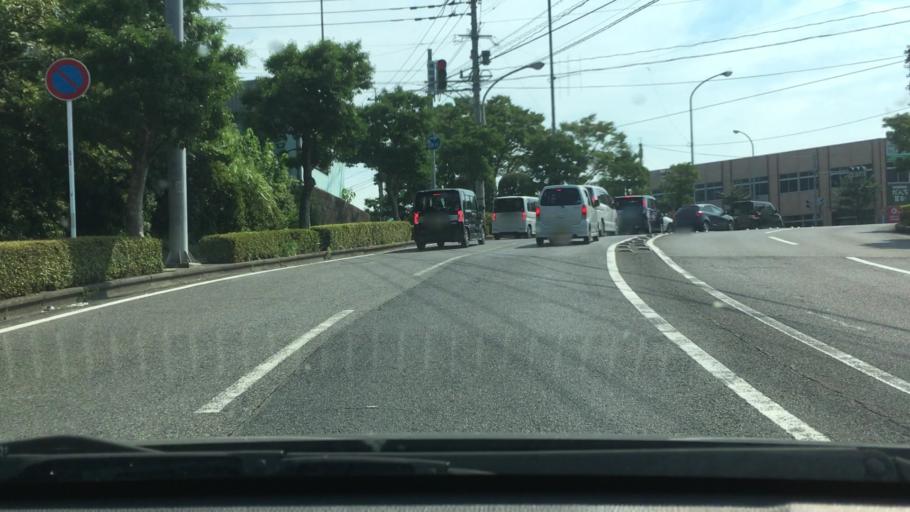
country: JP
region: Nagasaki
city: Sasebo
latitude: 33.1523
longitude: 129.7712
